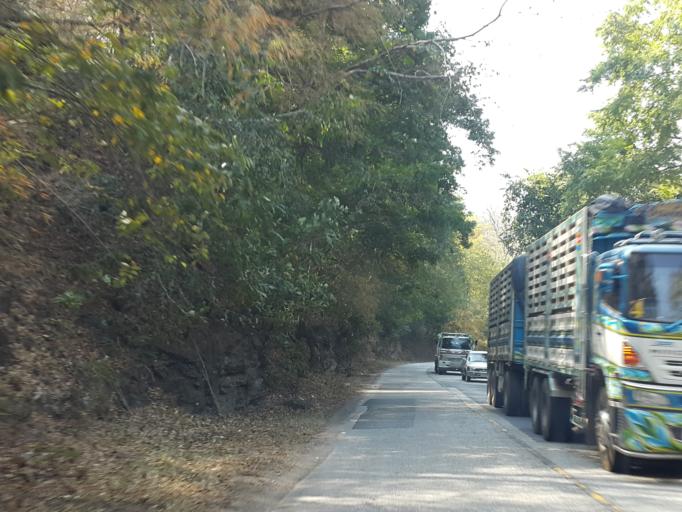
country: TH
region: Chiang Mai
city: Hot
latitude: 18.2317
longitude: 98.5235
